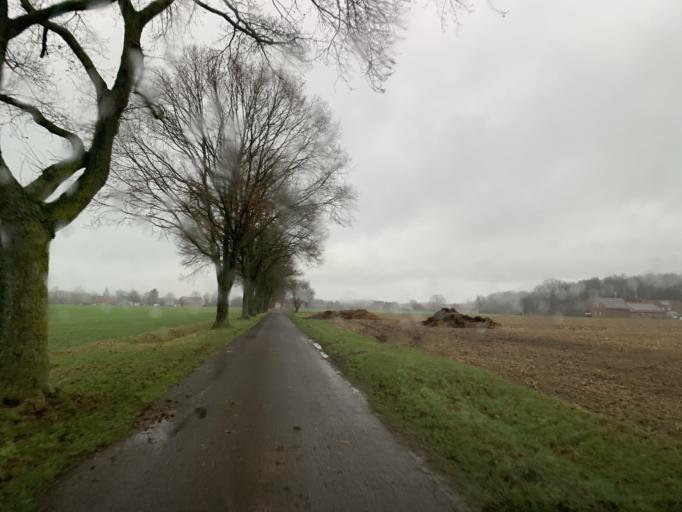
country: DE
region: North Rhine-Westphalia
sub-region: Regierungsbezirk Munster
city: Senden
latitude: 51.8964
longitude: 7.5322
